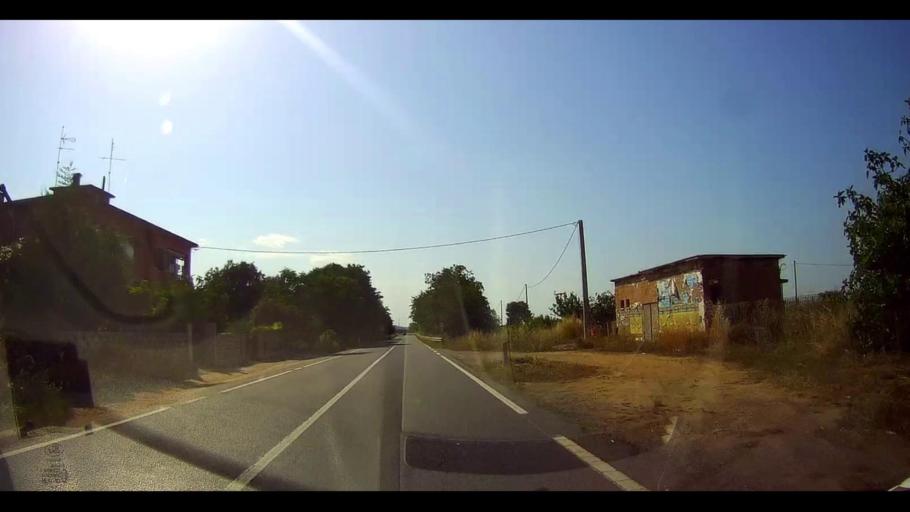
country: IT
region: Calabria
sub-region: Provincia di Crotone
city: Torretta
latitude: 39.4772
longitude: 17.0008
